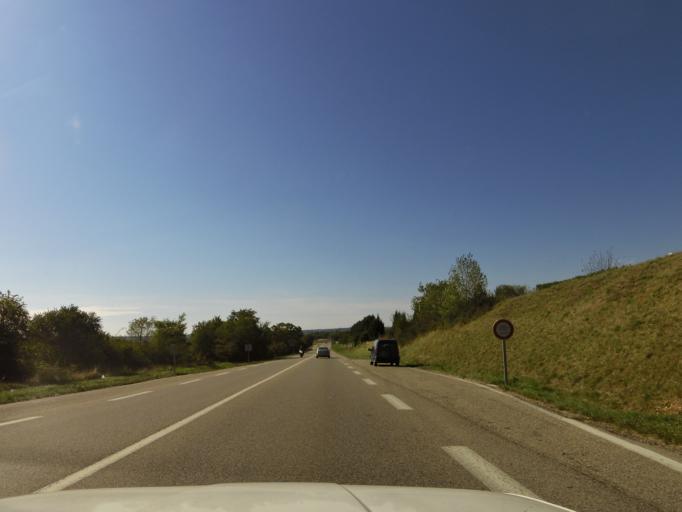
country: FR
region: Rhone-Alpes
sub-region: Departement de l'Ain
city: Saint-Denis-en-Bugey
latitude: 45.9433
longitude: 5.3260
